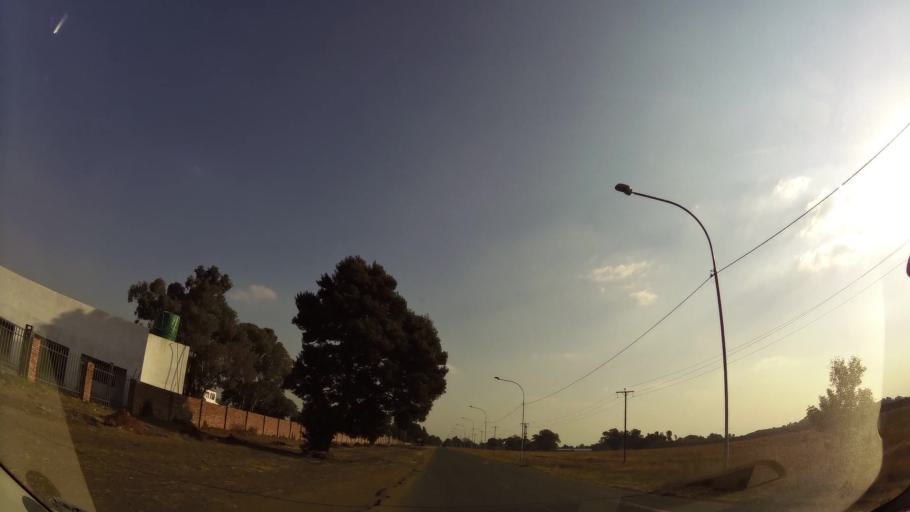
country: ZA
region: Gauteng
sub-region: Ekurhuleni Metropolitan Municipality
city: Benoni
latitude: -26.1027
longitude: 28.3829
